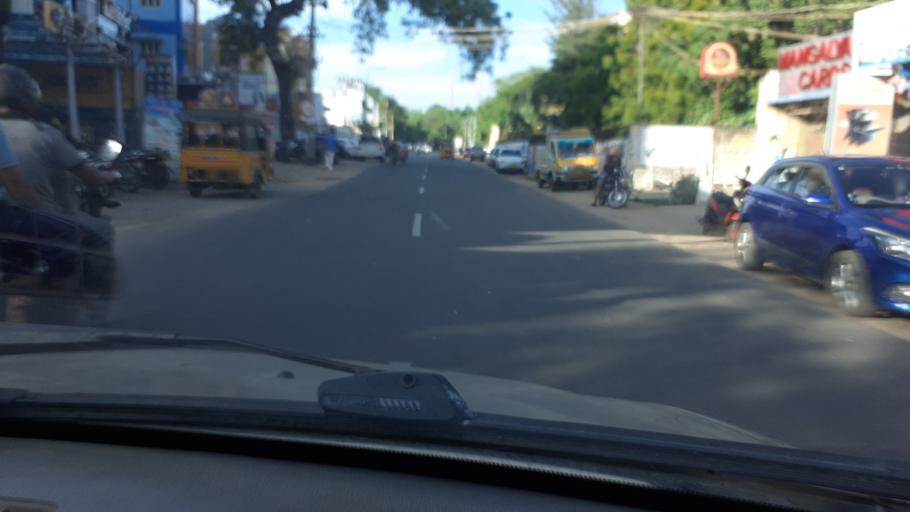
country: IN
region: Tamil Nadu
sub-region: Tirunelveli Kattabo
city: Tirunelveli
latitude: 8.7157
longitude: 77.7324
